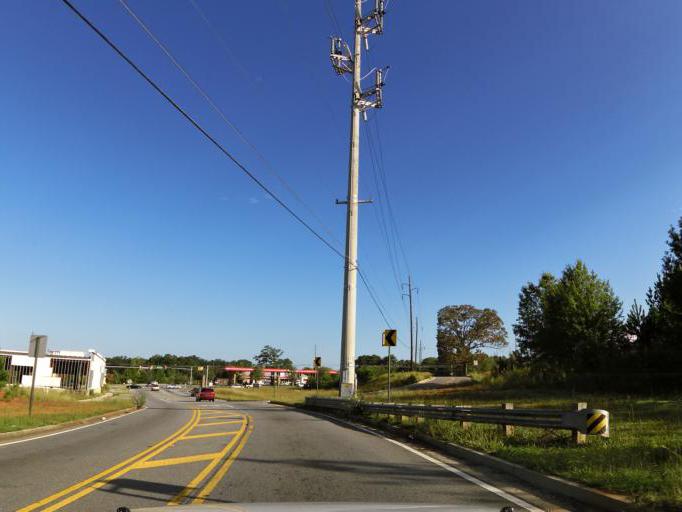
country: US
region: Georgia
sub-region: Cobb County
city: Powder Springs
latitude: 33.8648
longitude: -84.6326
